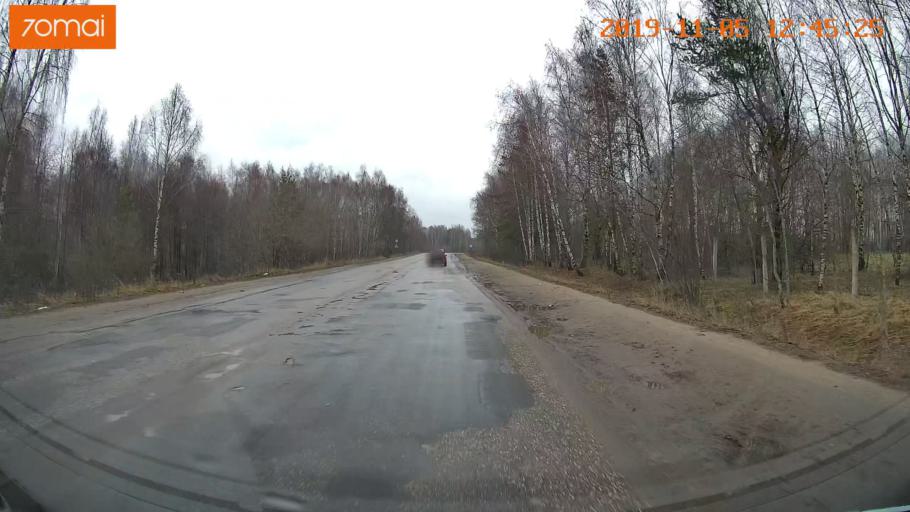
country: RU
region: Ivanovo
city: Kokhma
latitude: 56.9664
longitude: 41.0650
